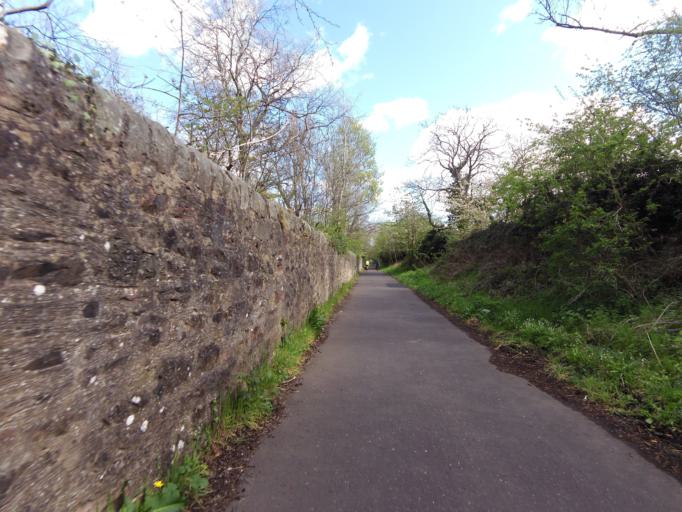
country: GB
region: Scotland
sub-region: West Lothian
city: Seafield
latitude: 55.9382
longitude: -3.1546
